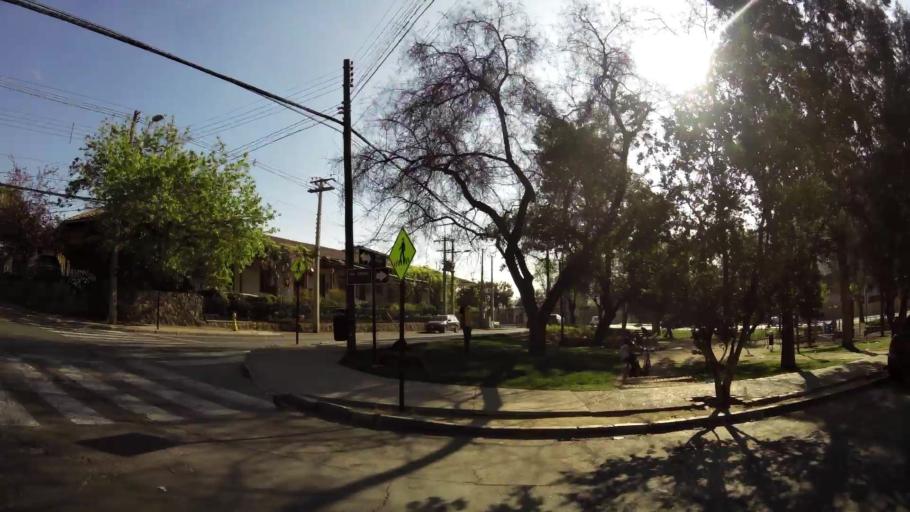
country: CL
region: Santiago Metropolitan
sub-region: Provincia de Santiago
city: Villa Presidente Frei, Nunoa, Santiago, Chile
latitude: -33.3636
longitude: -70.4933
